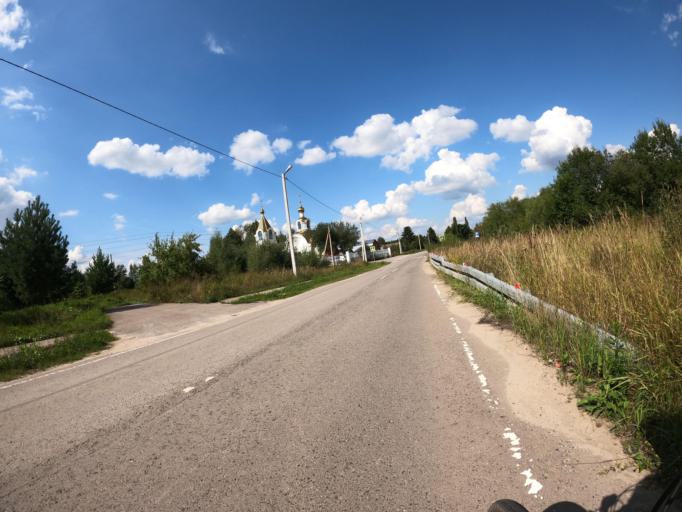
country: RU
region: Moskovskaya
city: Troitskoye
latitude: 55.2560
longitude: 38.5783
